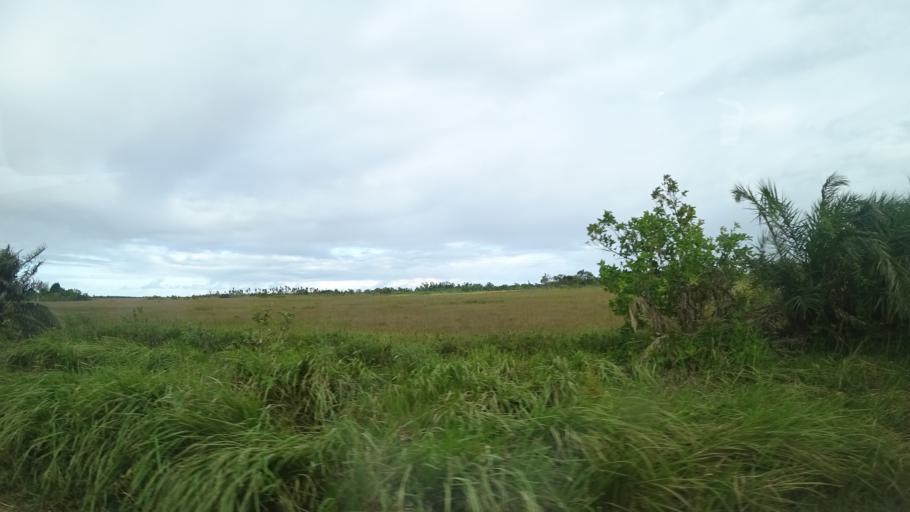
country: MZ
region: Sofala
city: Beira
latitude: -19.7117
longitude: 35.0149
